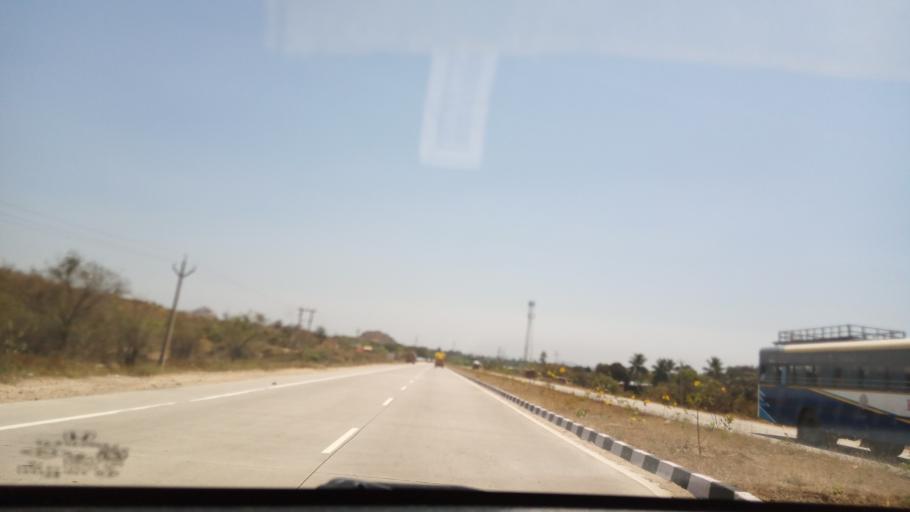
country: IN
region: Andhra Pradesh
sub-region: Chittoor
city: Chittoor
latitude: 13.2012
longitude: 78.9657
